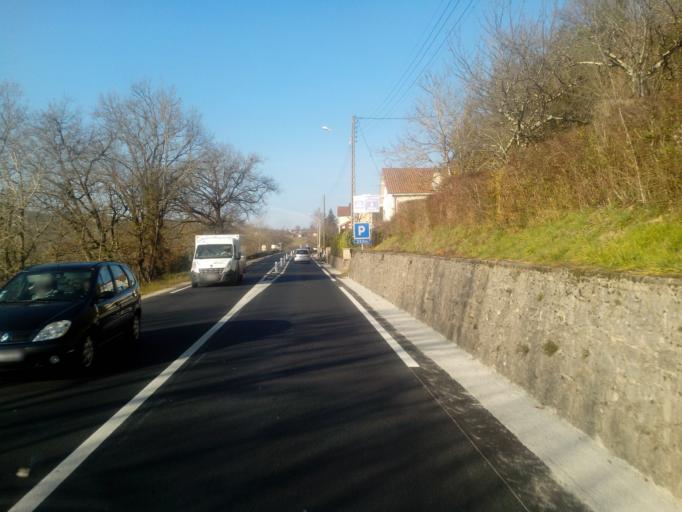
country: FR
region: Midi-Pyrenees
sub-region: Departement de l'Aveyron
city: Capdenac-Gare
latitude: 44.5806
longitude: 2.0668
